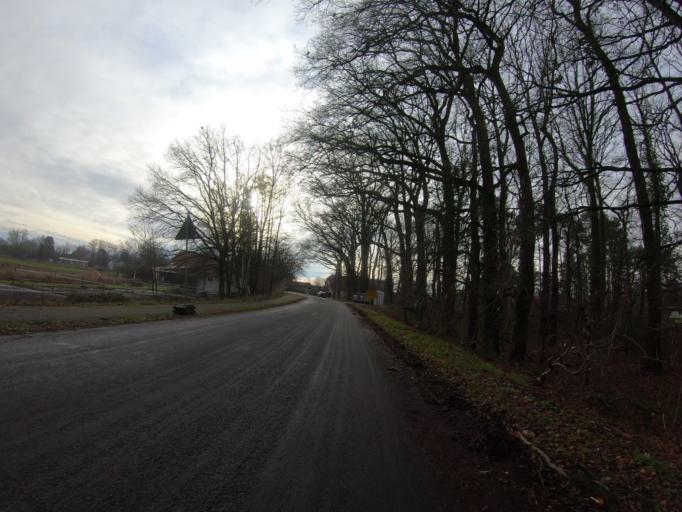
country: DE
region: Lower Saxony
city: Muden
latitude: 52.5043
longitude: 10.4093
